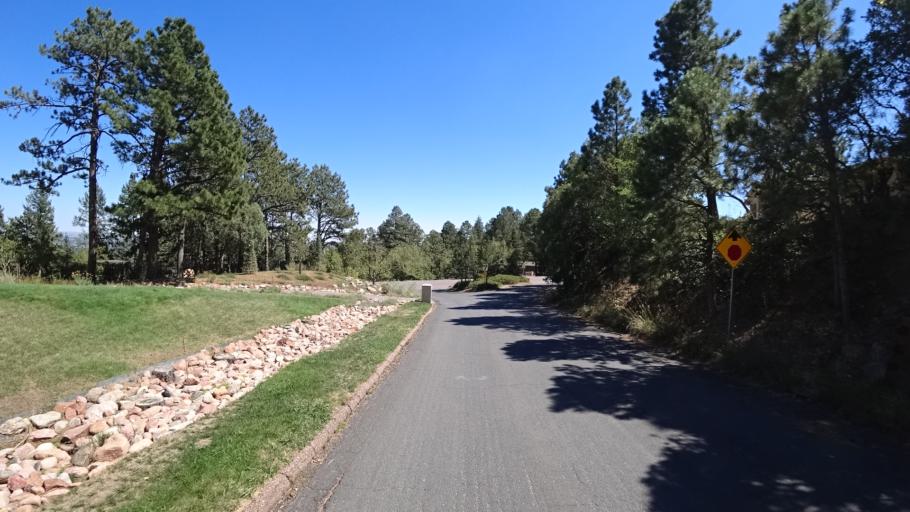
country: US
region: Colorado
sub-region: El Paso County
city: Colorado Springs
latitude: 38.7802
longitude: -104.8551
